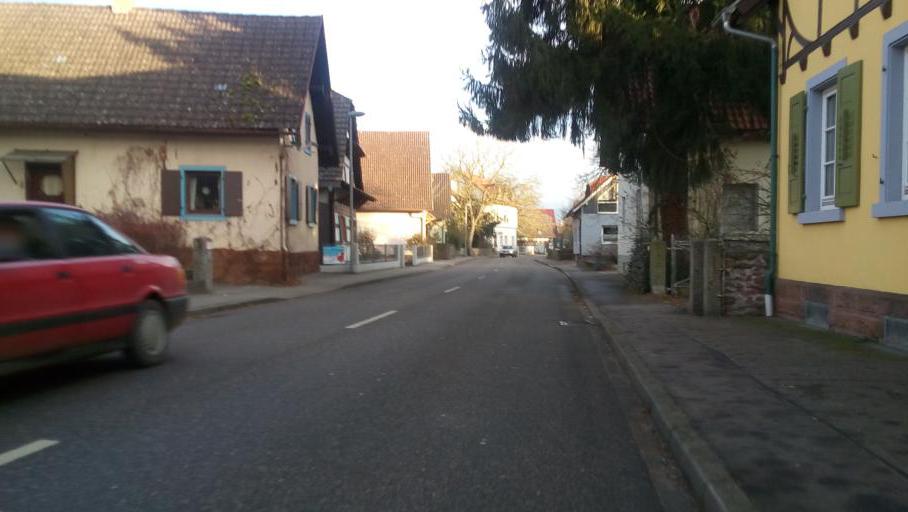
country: DE
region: Baden-Wuerttemberg
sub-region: Karlsruhe Region
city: Lichtenau
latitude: 48.6817
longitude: 7.9834
